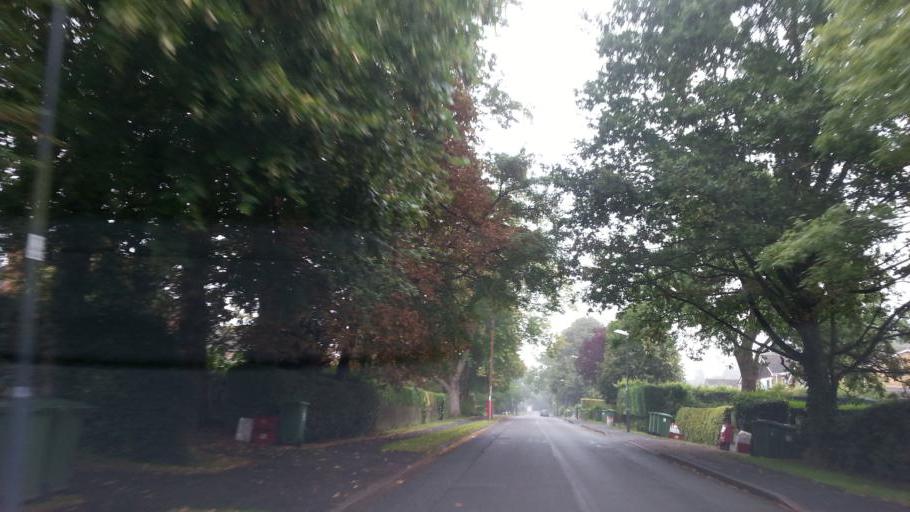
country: GB
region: England
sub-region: Warwickshire
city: Kenilworth
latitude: 52.3527
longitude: -1.5875
